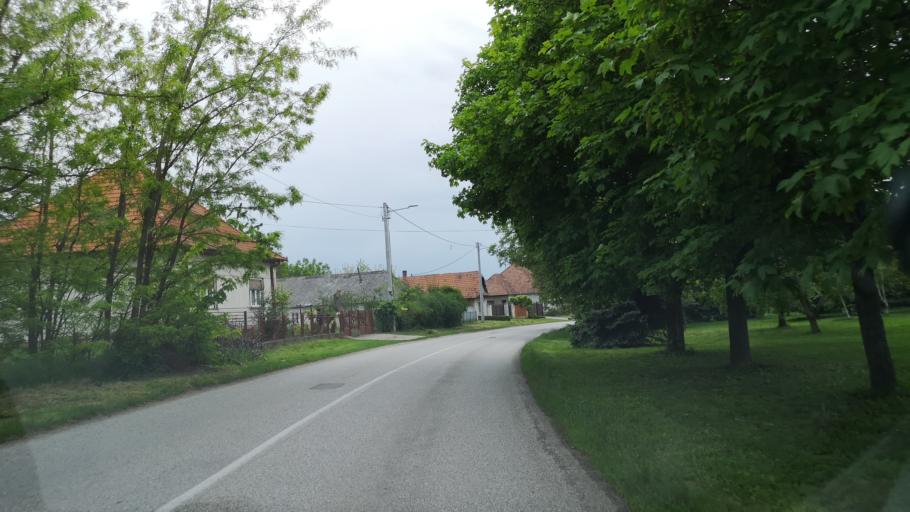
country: SK
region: Nitriansky
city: Sellye
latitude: 48.2552
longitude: 17.8729
